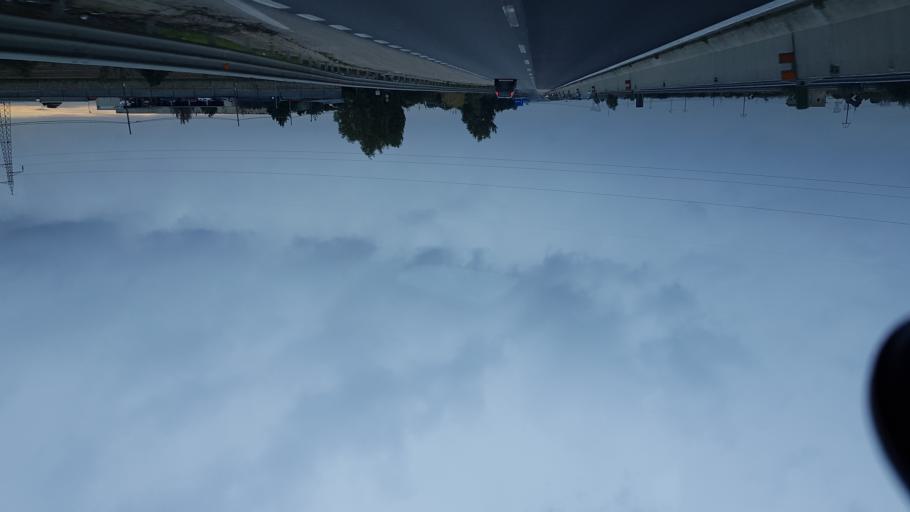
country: IT
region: Apulia
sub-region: Provincia di Brindisi
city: Brindisi
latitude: 40.6104
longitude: 17.8931
